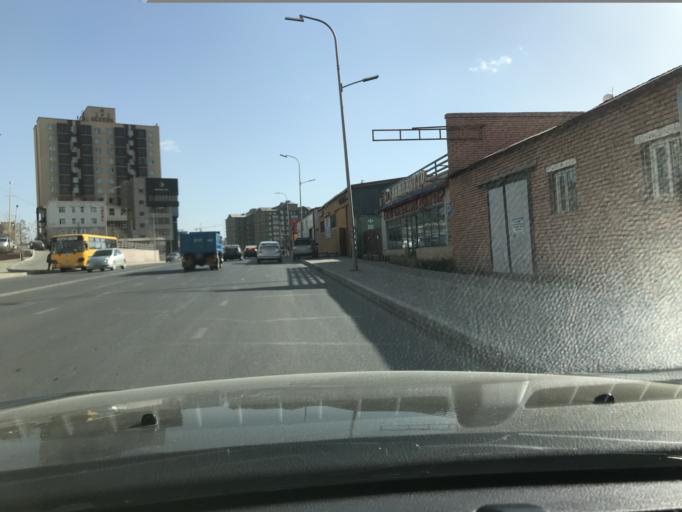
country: MN
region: Ulaanbaatar
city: Ulaanbaatar
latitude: 47.9251
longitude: 106.9462
